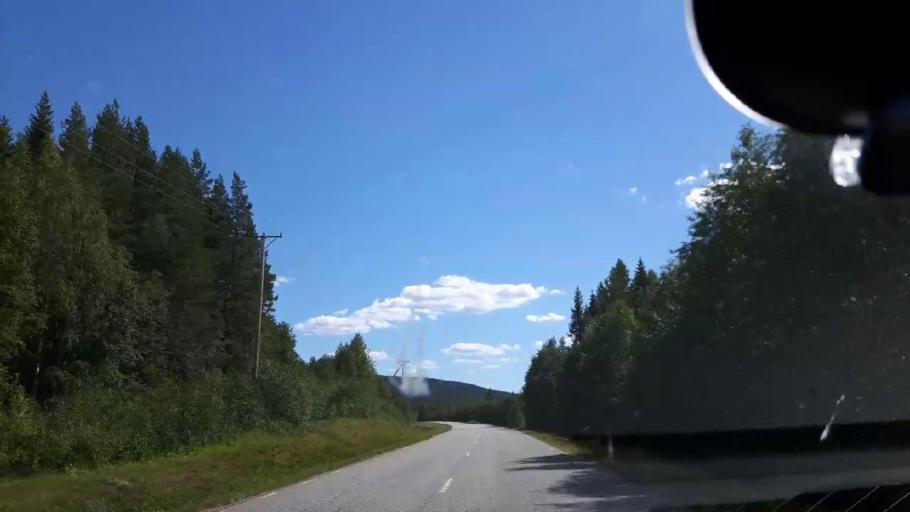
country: SE
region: Vaesternorrland
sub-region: Ange Kommun
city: Fransta
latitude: 62.7508
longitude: 16.3182
